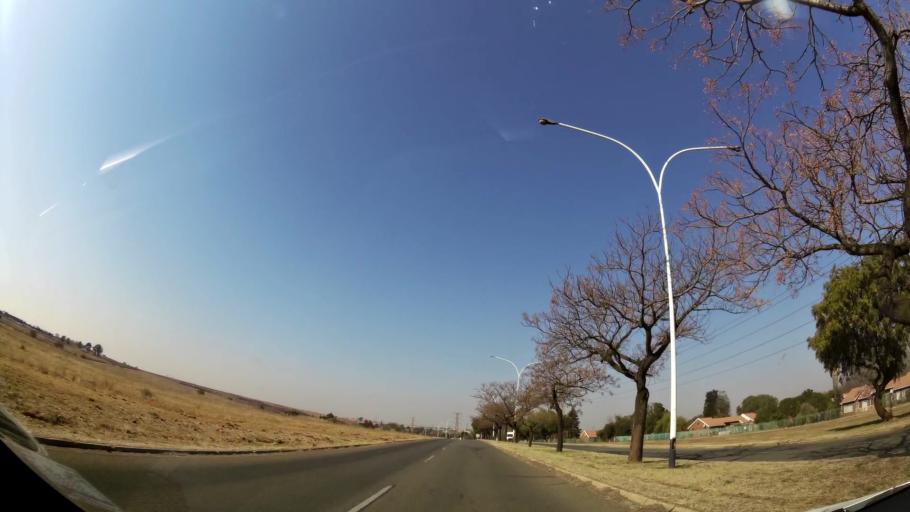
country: ZA
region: Gauteng
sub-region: Ekurhuleni Metropolitan Municipality
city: Boksburg
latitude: -26.2258
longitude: 28.2730
